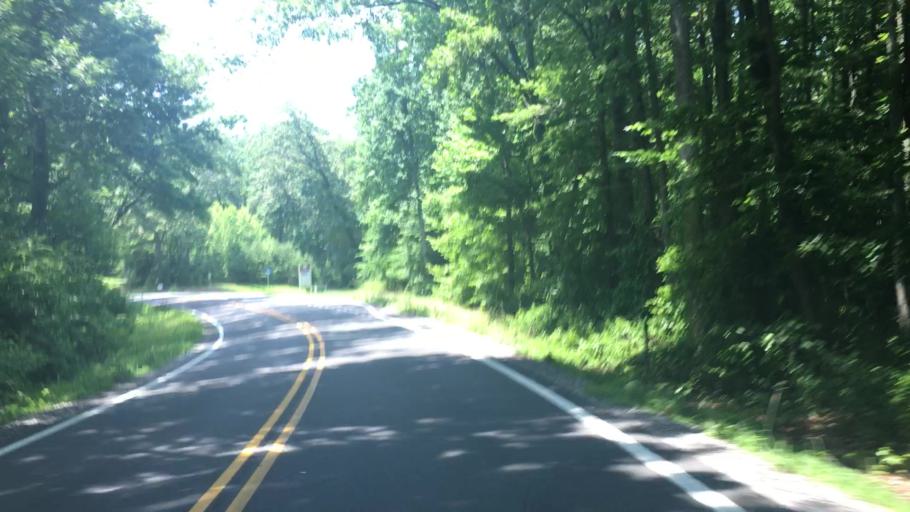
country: US
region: Virginia
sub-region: King George County
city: King George
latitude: 38.3179
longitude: -77.1931
